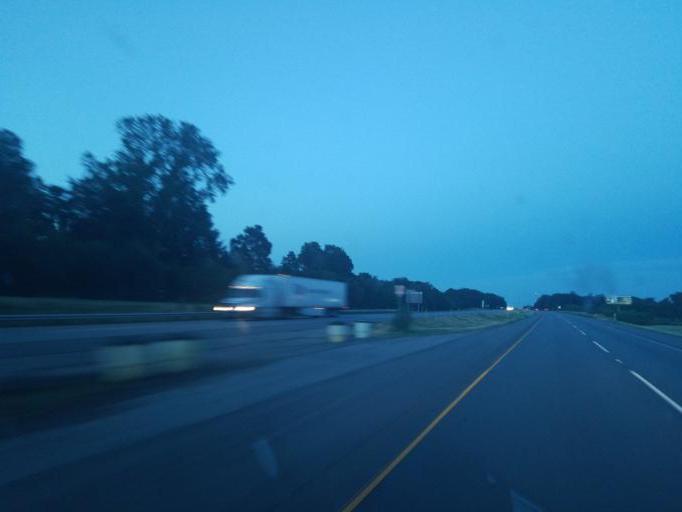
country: US
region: Indiana
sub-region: Saint Joseph County
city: Georgetown
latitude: 41.7160
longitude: -86.2164
